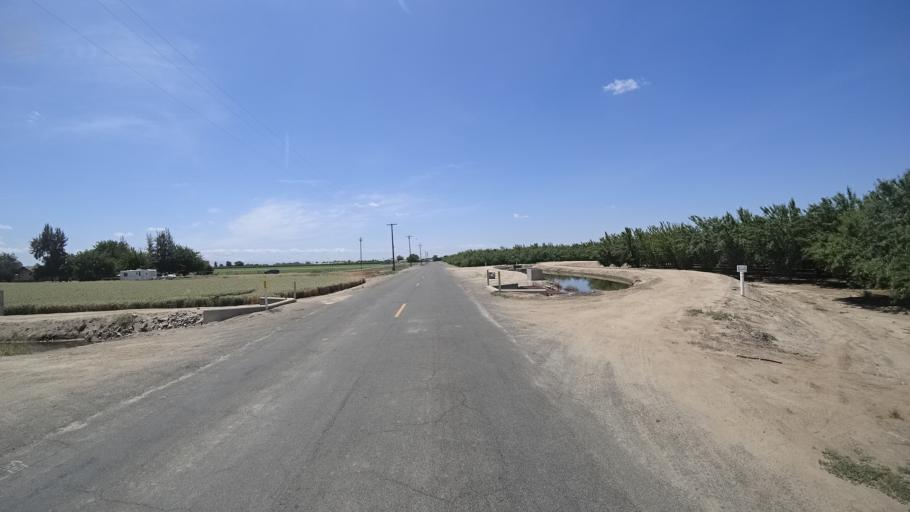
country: US
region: California
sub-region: Kings County
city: Lemoore
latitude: 36.2840
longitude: -119.7477
